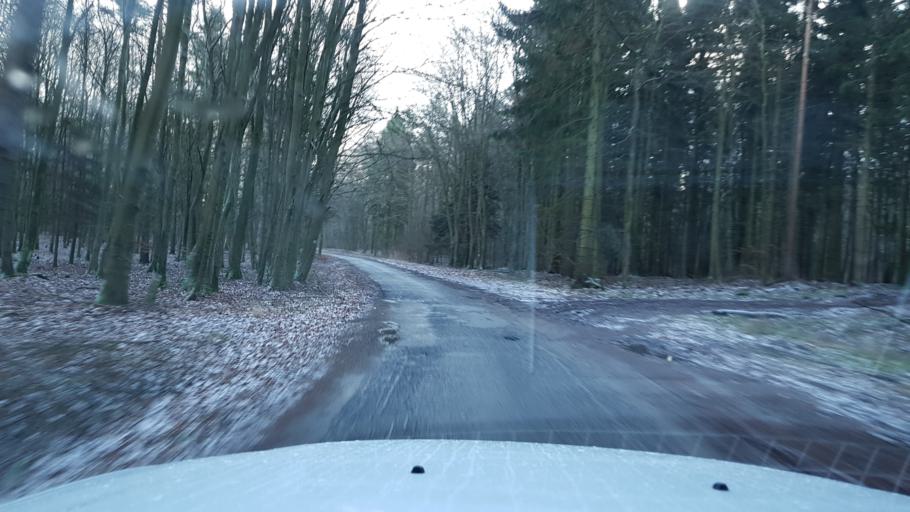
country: PL
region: West Pomeranian Voivodeship
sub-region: Powiat gryficki
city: Trzebiatow
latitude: 54.0434
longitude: 15.3308
